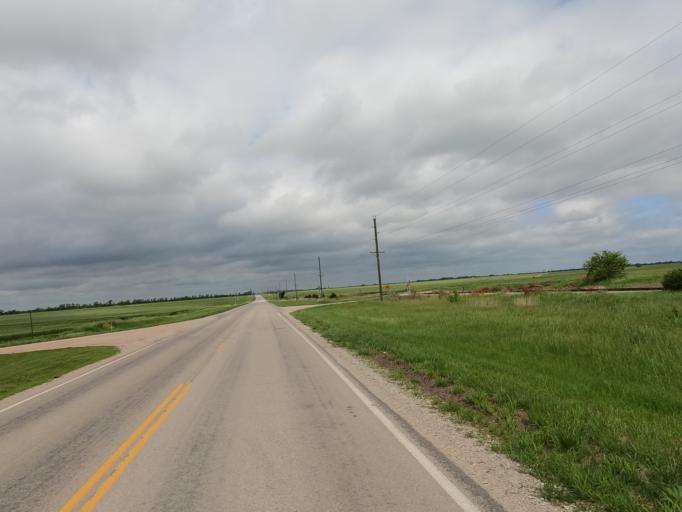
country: US
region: Kansas
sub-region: McPherson County
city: McPherson
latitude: 38.2938
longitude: -97.6299
